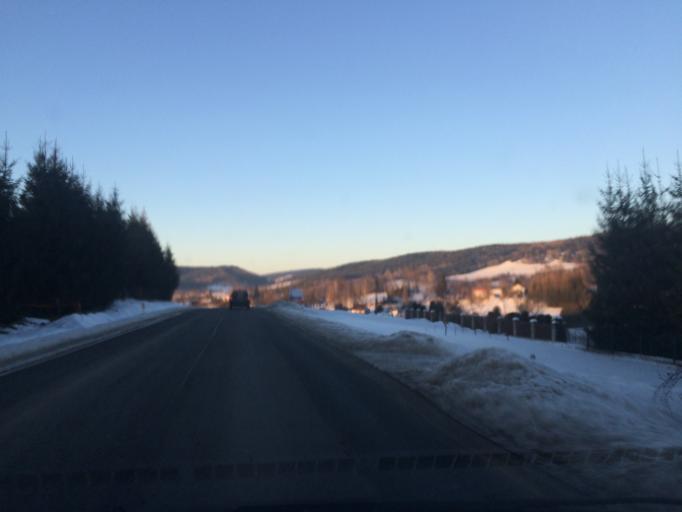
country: PL
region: Subcarpathian Voivodeship
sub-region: Powiat bieszczadzki
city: Czarna
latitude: 49.3156
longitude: 22.6728
